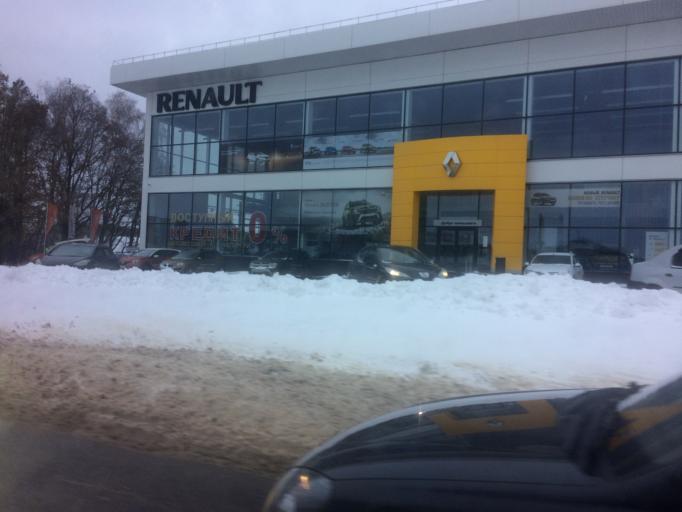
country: RU
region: Tula
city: Tula
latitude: 54.1594
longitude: 37.6371
